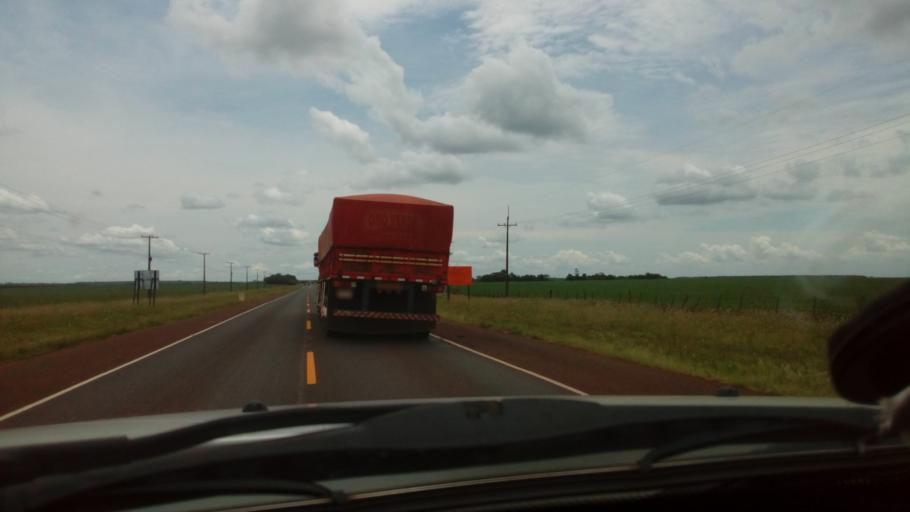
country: PY
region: Alto Parana
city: Colonia Yguazu
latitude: -25.5788
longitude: -54.9234
